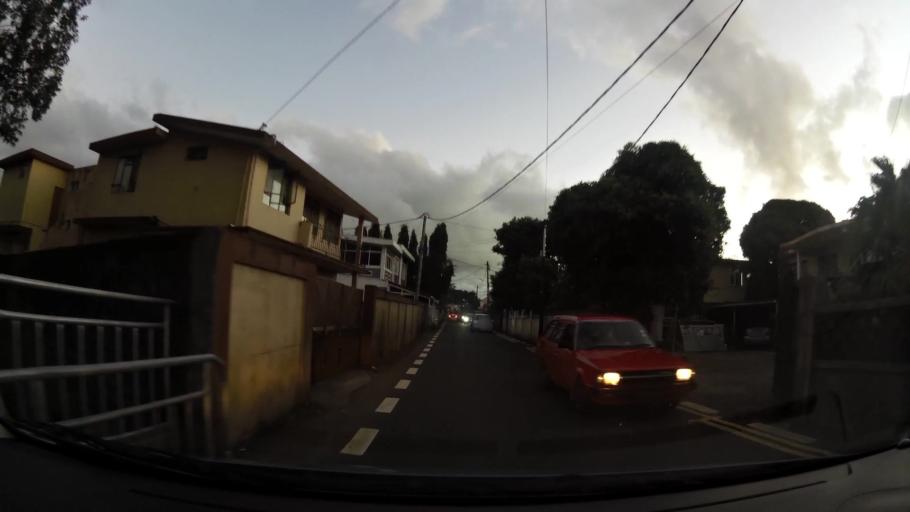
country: MU
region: Plaines Wilhems
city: Curepipe
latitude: -20.2925
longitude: 57.5204
